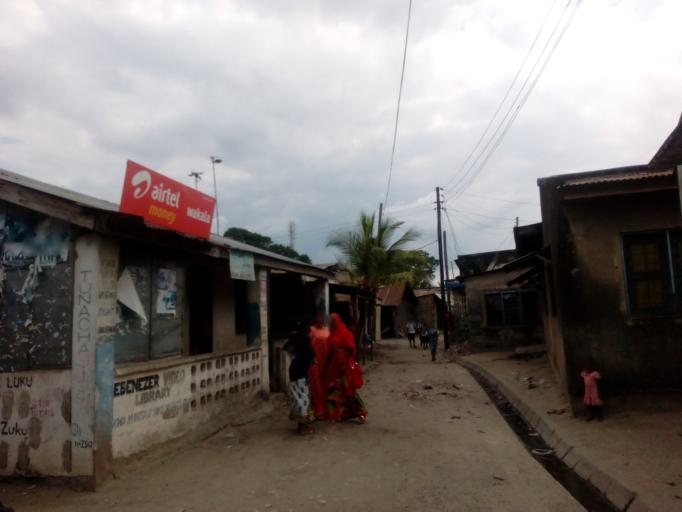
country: TZ
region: Dar es Salaam
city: Dar es Salaam
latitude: -6.8564
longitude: 39.2501
